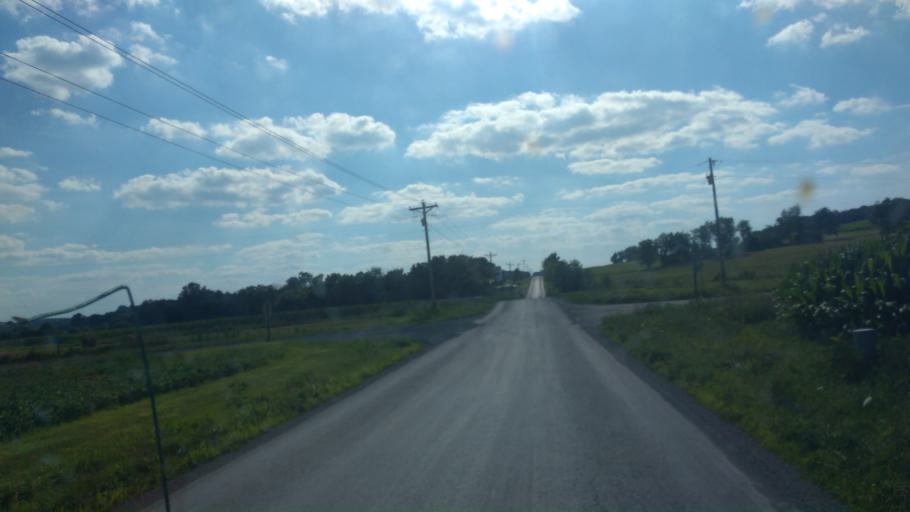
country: US
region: Ohio
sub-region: Wayne County
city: Apple Creek
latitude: 40.7262
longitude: -81.8621
